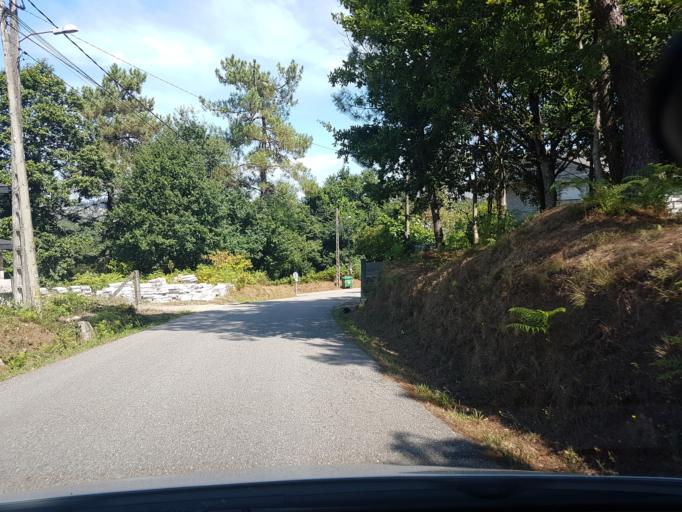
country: ES
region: Galicia
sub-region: Provincia de Pontevedra
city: Porrino
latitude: 42.1966
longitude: -8.6217
